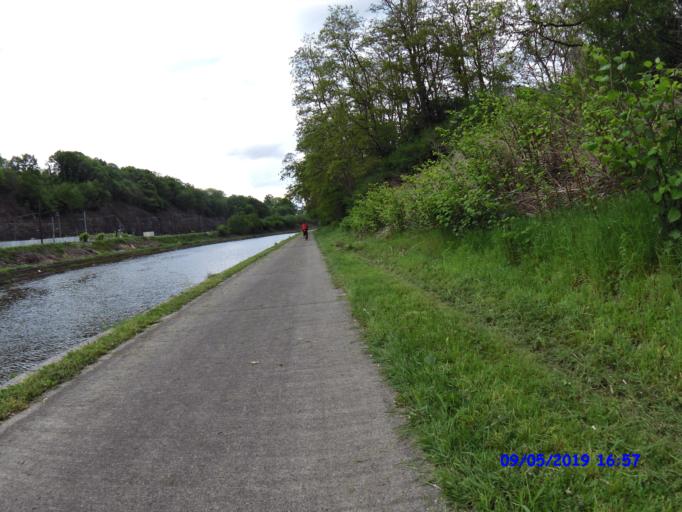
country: BE
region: Wallonia
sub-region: Province de Namur
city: Namur
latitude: 50.4618
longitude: 4.8328
